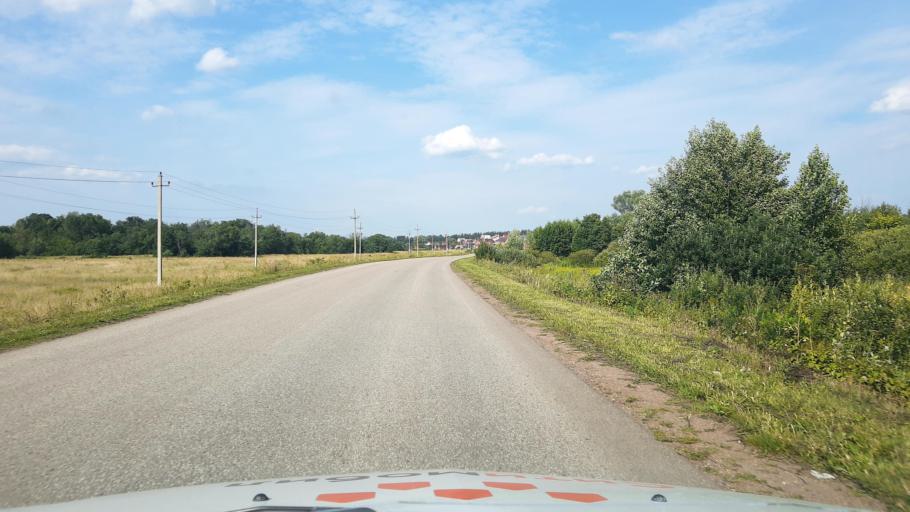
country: RU
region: Bashkortostan
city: Kabakovo
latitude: 54.6628
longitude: 56.2037
